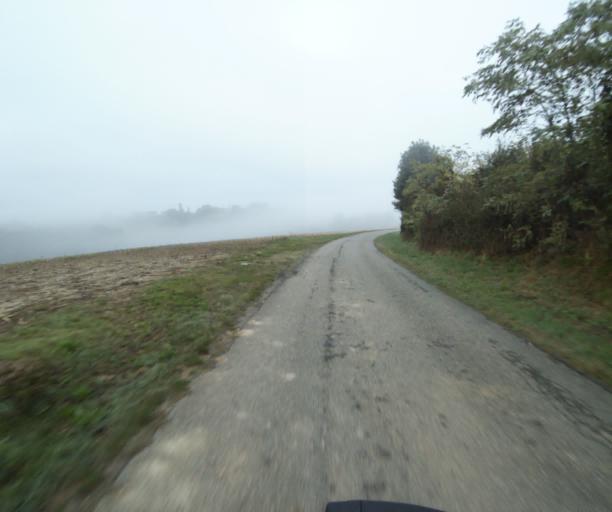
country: FR
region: Midi-Pyrenees
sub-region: Departement du Tarn-et-Garonne
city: Saint-Nauphary
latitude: 43.9448
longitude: 1.4085
